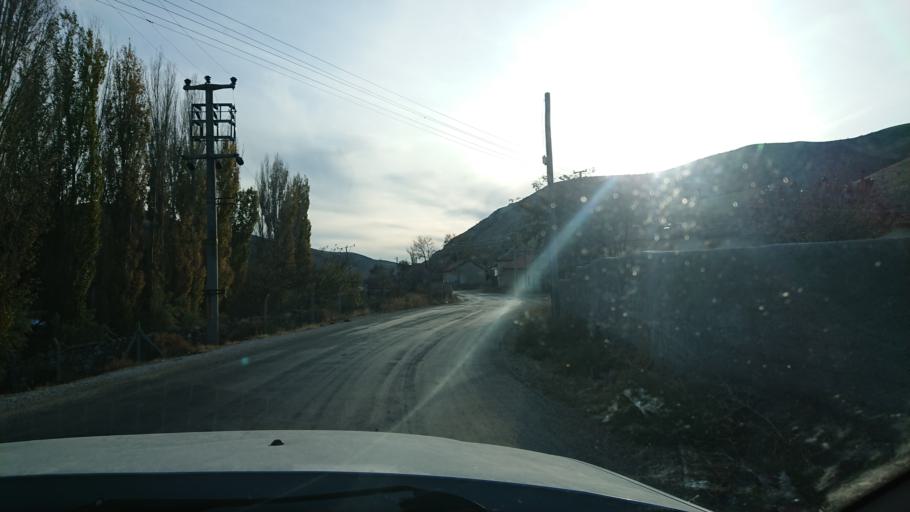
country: TR
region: Ankara
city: Sereflikochisar
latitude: 38.7645
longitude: 33.6991
